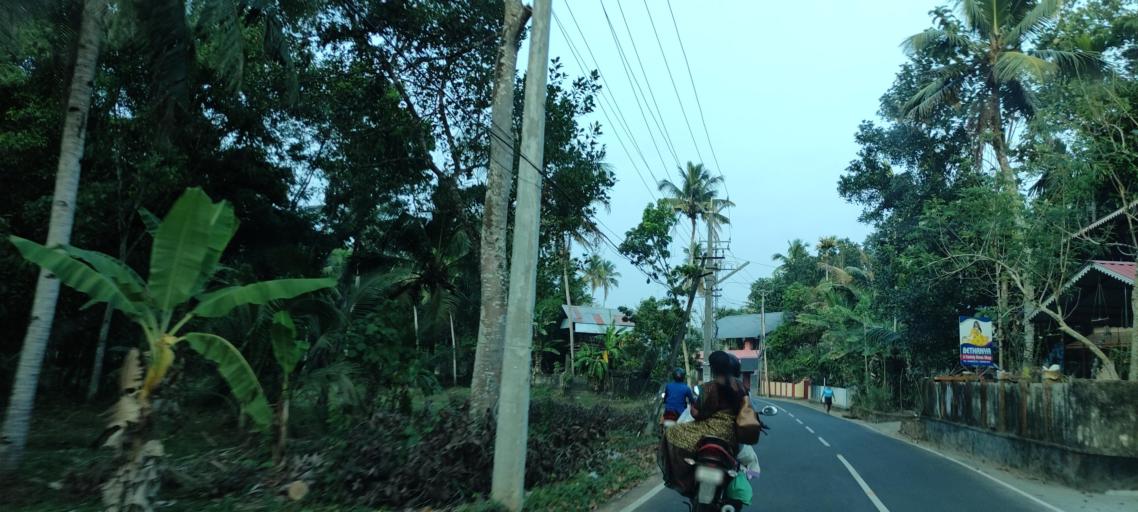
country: IN
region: Kerala
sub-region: Alappuzha
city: Mavelikara
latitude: 9.2695
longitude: 76.5560
